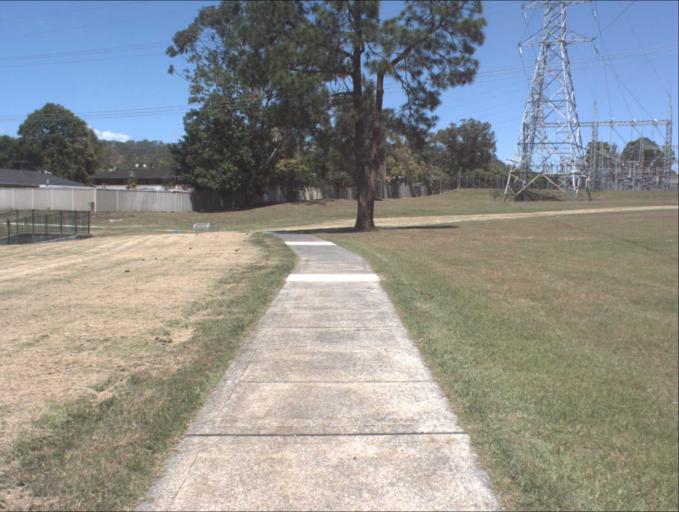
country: AU
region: Queensland
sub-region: Gold Coast
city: Yatala
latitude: -27.7250
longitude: 153.2099
